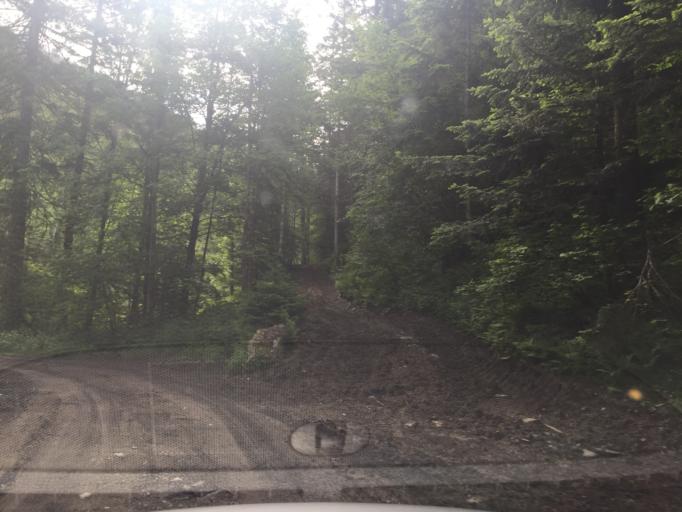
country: FR
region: Rhone-Alpes
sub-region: Departement de la Savoie
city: La Rochette
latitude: 45.4364
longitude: 6.1627
